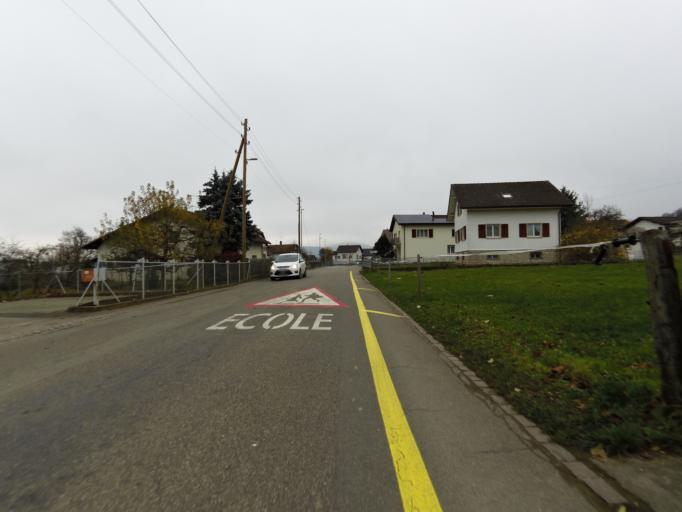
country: CH
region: Jura
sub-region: Porrentruy District
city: Alle
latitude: 47.4078
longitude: 7.1627
